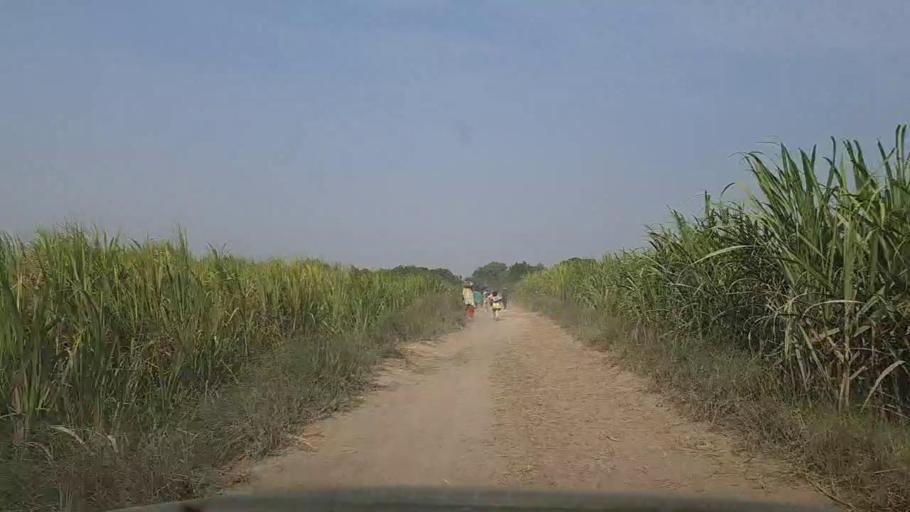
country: PK
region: Sindh
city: Bulri
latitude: 25.0220
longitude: 68.2816
